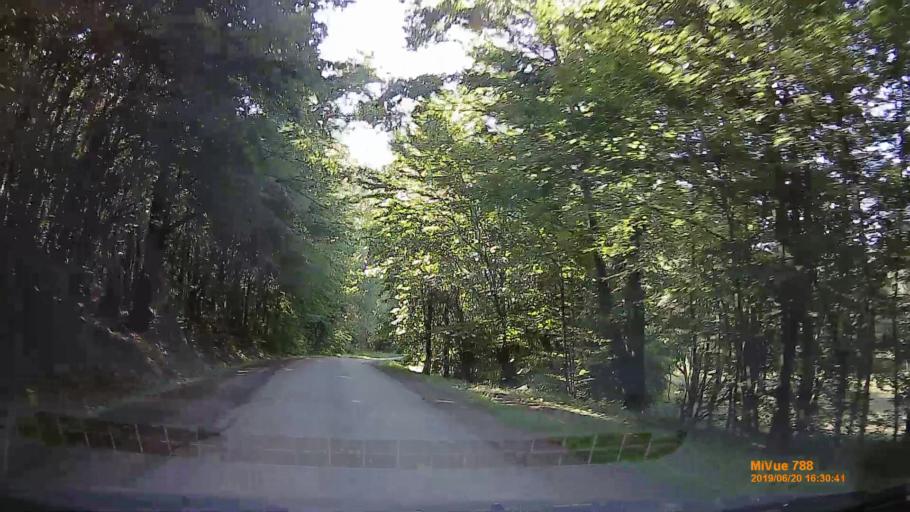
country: HU
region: Baranya
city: Buekkoesd
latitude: 46.1703
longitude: 18.0541
